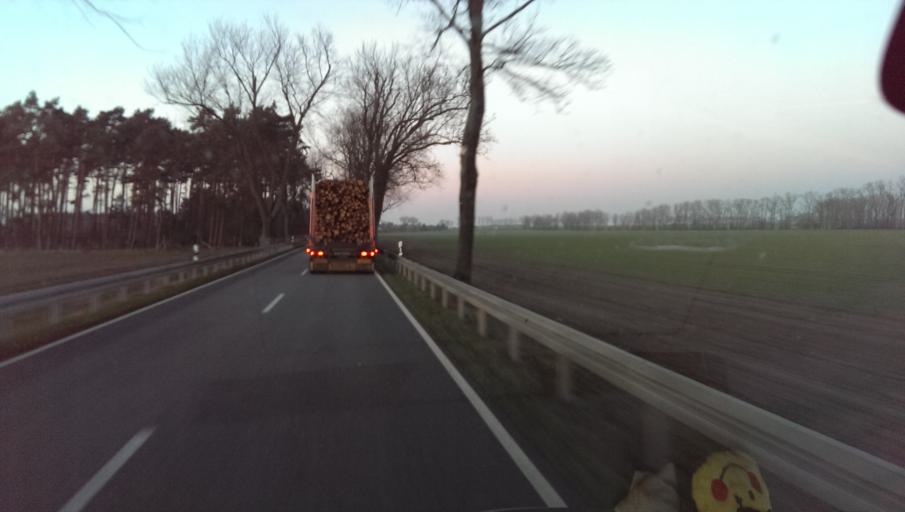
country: DE
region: Saxony-Anhalt
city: Holzdorf
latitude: 51.8904
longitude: 13.1415
